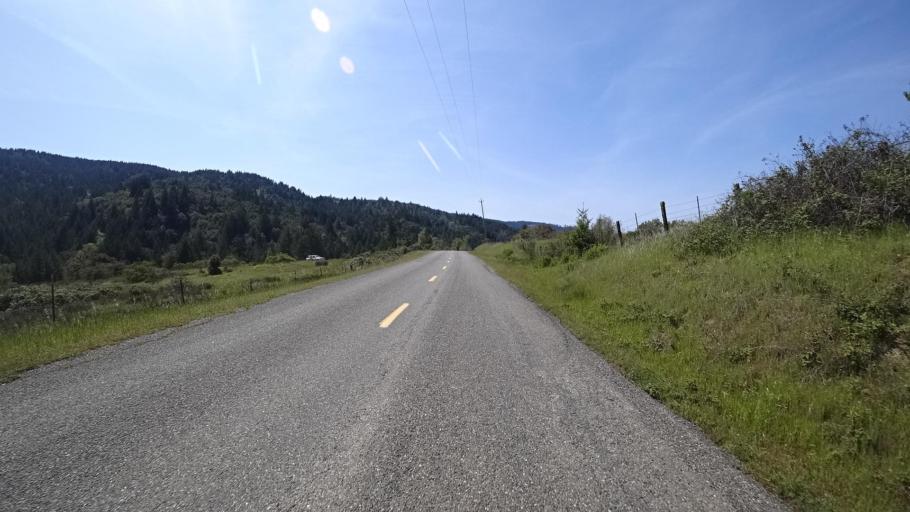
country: US
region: California
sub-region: Humboldt County
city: Redway
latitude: 40.3400
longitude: -123.7016
